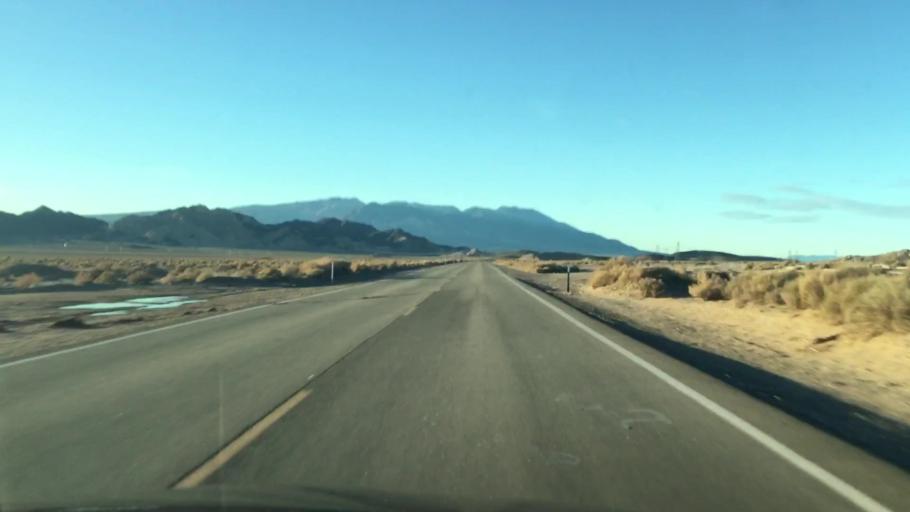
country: US
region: California
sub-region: San Bernardino County
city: Fort Irwin
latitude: 35.3708
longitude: -116.1159
